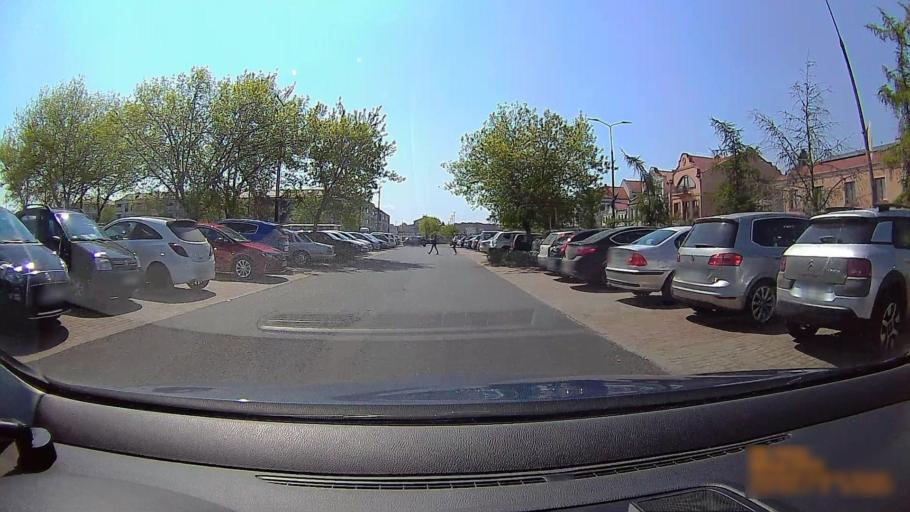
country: PL
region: Greater Poland Voivodeship
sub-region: Konin
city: Konin
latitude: 52.2104
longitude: 18.2572
